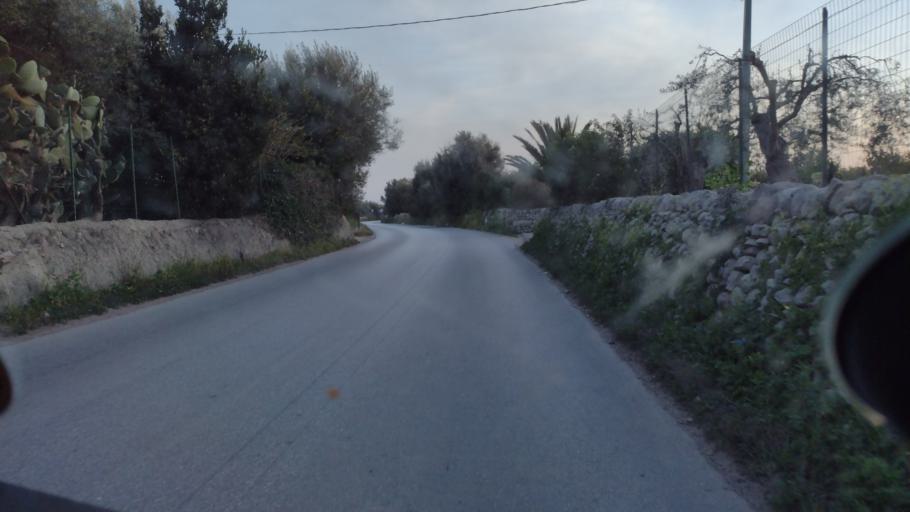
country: IT
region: Sicily
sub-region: Provincia di Siracusa
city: Avola
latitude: 36.8888
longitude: 15.1317
